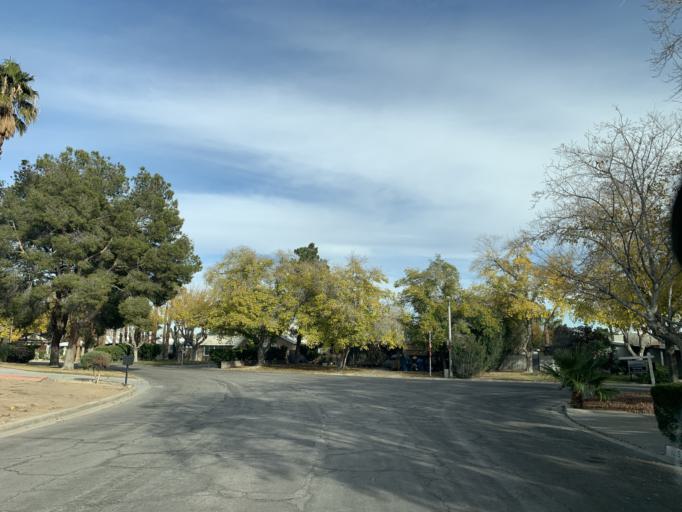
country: US
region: Nevada
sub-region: Clark County
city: Las Vegas
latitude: 36.1487
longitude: -115.1719
